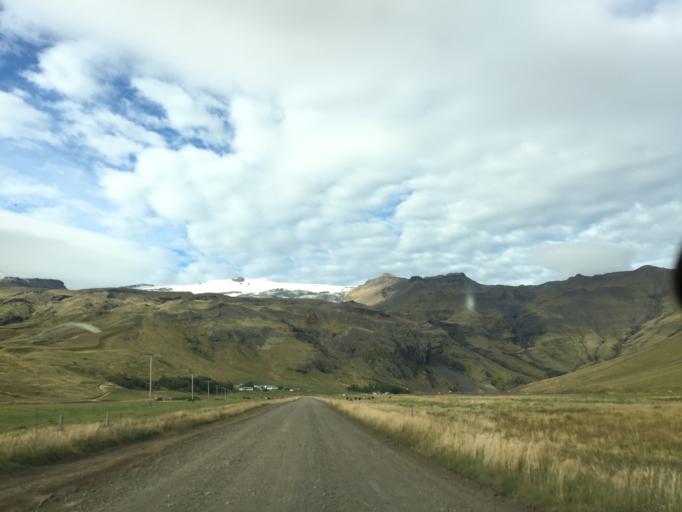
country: IS
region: South
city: Vestmannaeyjar
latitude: 63.5512
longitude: -19.6272
